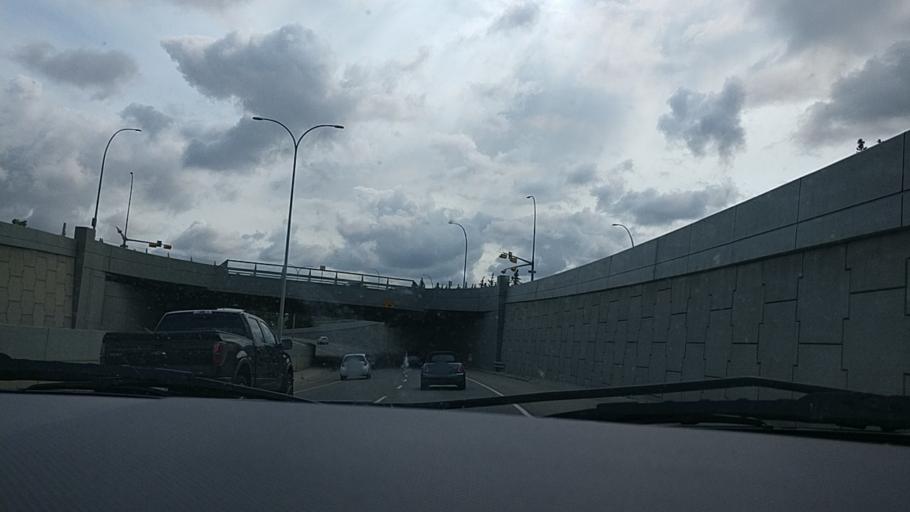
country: CA
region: Alberta
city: Calgary
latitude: 51.0898
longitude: -114.0961
